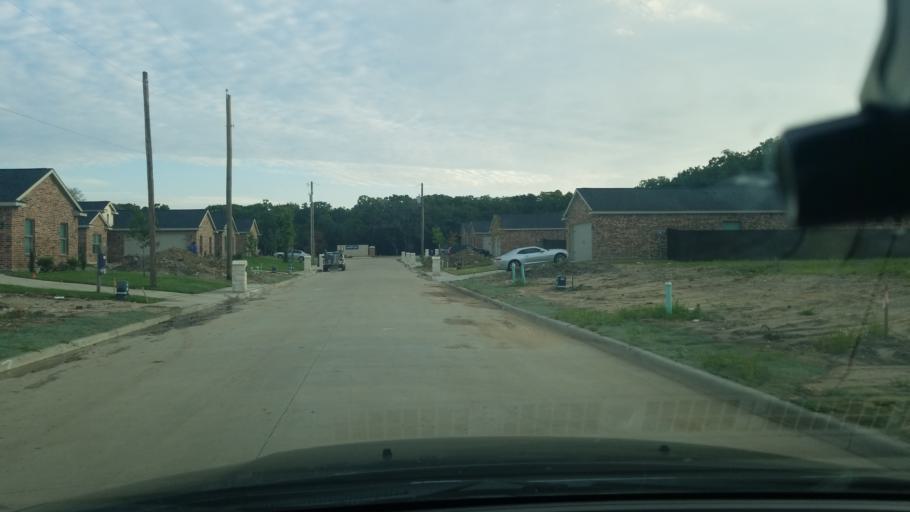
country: US
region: Texas
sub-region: Dallas County
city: Balch Springs
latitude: 32.7364
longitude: -96.6361
